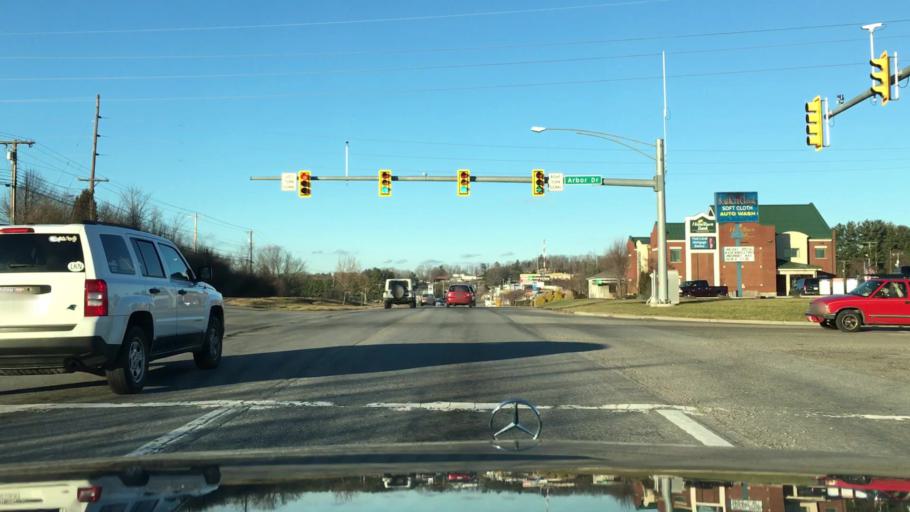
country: US
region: Virginia
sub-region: Montgomery County
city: Merrimac
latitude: 37.1691
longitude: -80.4213
